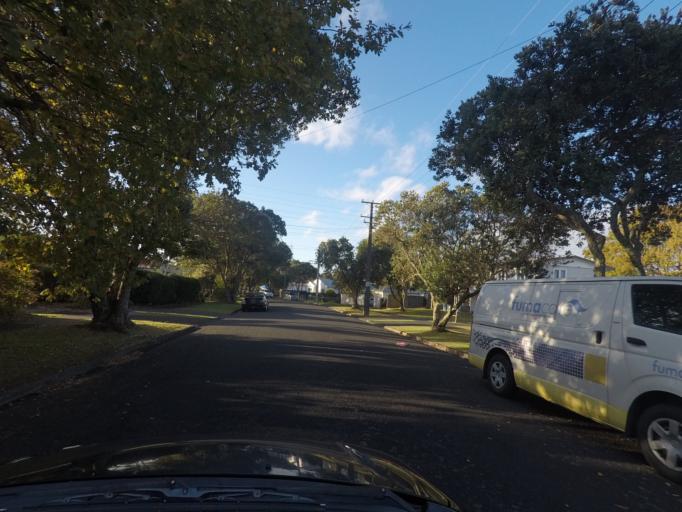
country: NZ
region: Auckland
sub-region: Auckland
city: Waitakere
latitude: -36.9001
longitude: 174.6767
